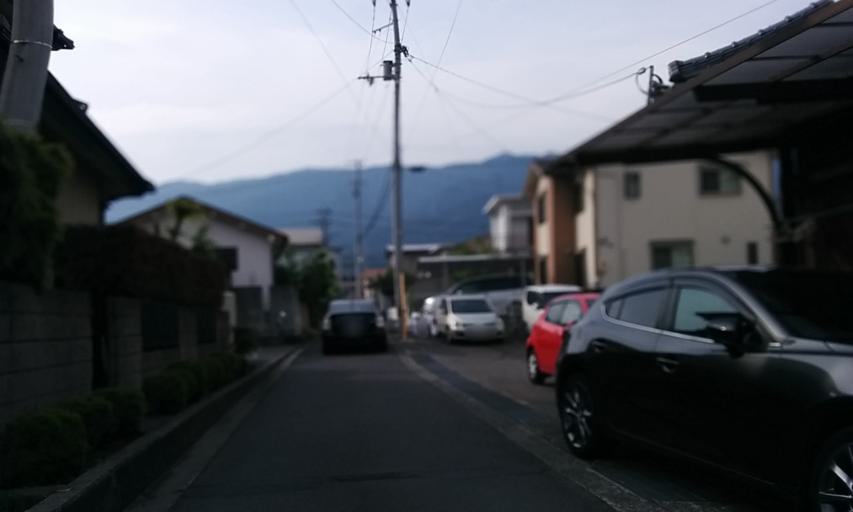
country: JP
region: Ehime
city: Kawanoecho
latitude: 33.9838
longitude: 133.5542
